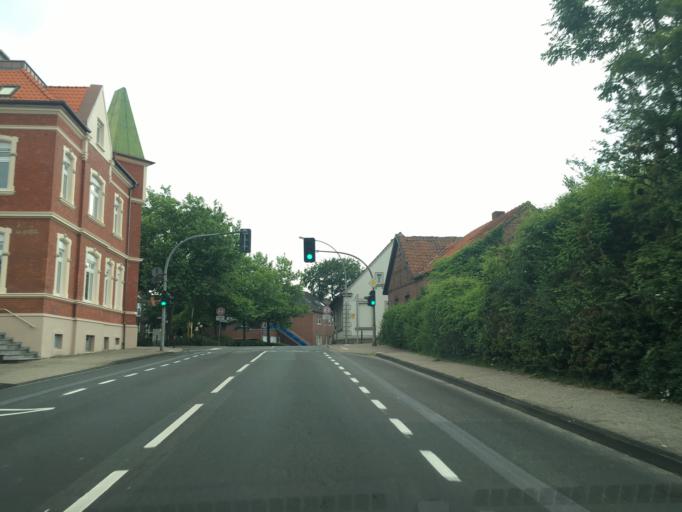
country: DE
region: North Rhine-Westphalia
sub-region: Regierungsbezirk Munster
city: Altenberge
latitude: 52.0470
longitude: 7.4703
